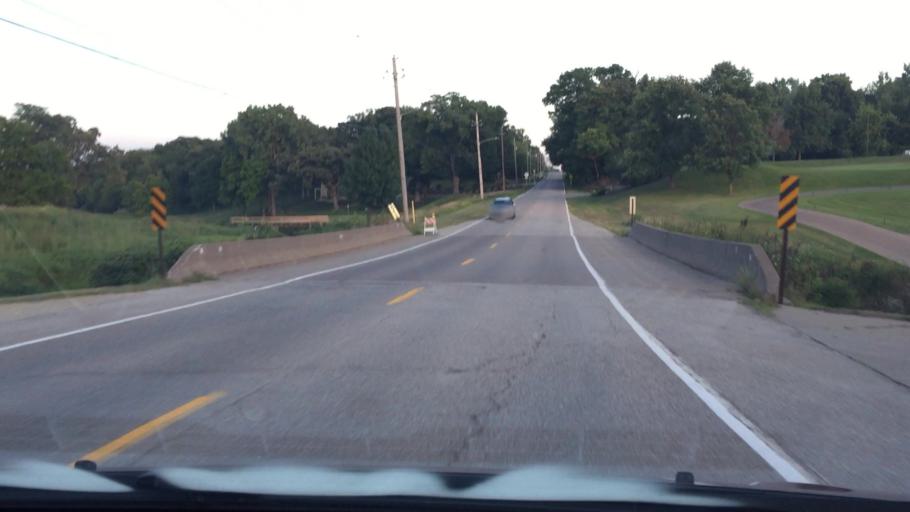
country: US
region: Iowa
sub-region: Muscatine County
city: Muscatine
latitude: 41.4494
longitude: -91.0555
